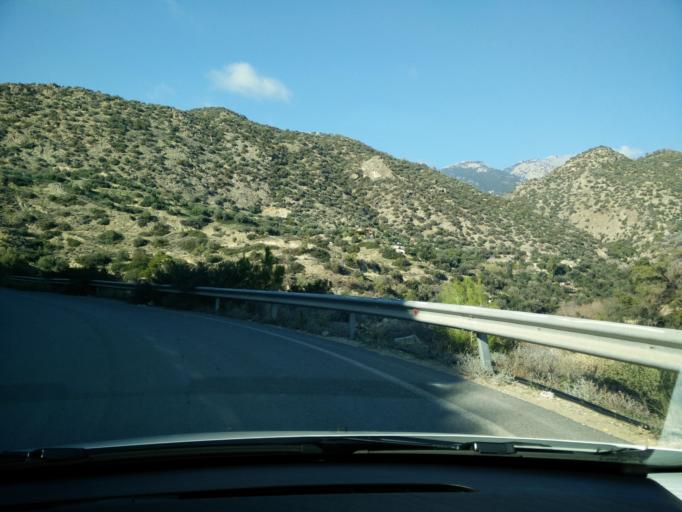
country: GR
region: Crete
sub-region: Nomos Lasithiou
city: Gra Liyia
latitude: 34.9954
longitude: 25.5327
